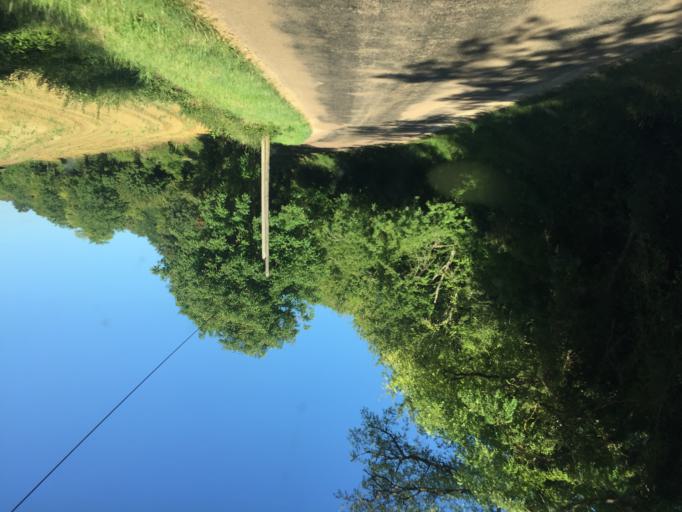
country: FR
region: Bourgogne
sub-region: Departement de l'Yonne
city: Fontenailles
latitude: 47.4825
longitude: 3.4015
